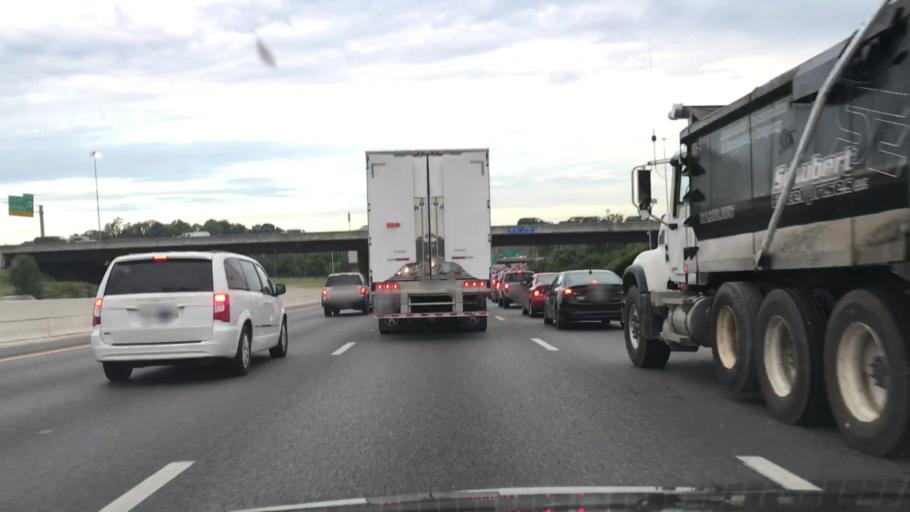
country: US
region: Tennessee
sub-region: Davidson County
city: Oak Hill
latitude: 36.1090
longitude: -86.7201
